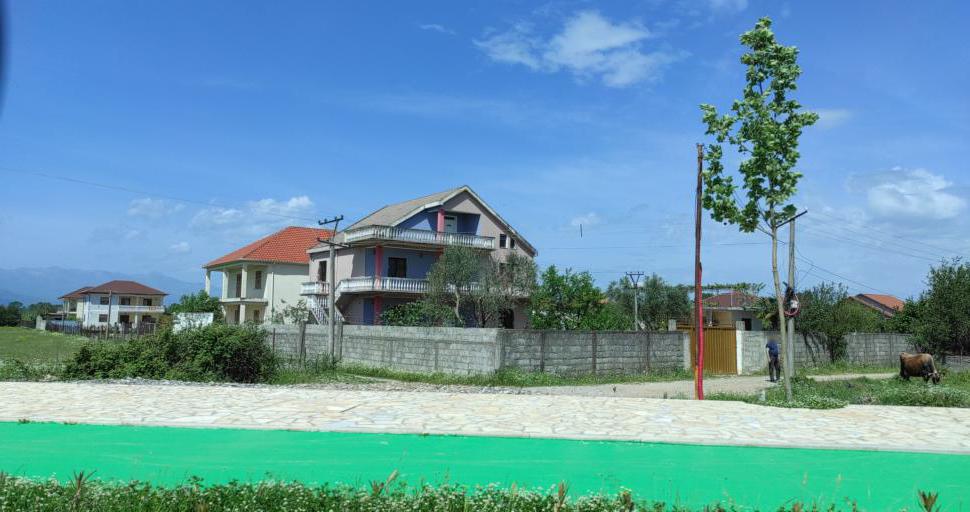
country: AL
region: Shkoder
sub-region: Rrethi i Shkodres
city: Shkoder
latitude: 42.0853
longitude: 19.5033
